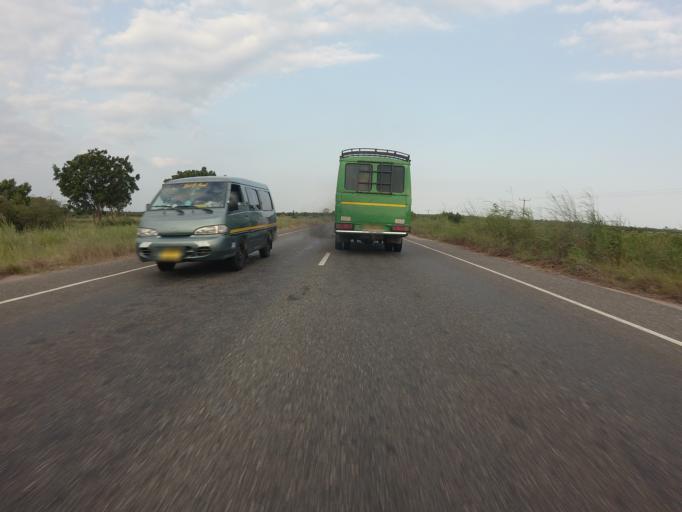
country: GH
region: Volta
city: Anloga
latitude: 6.0894
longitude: 0.5340
